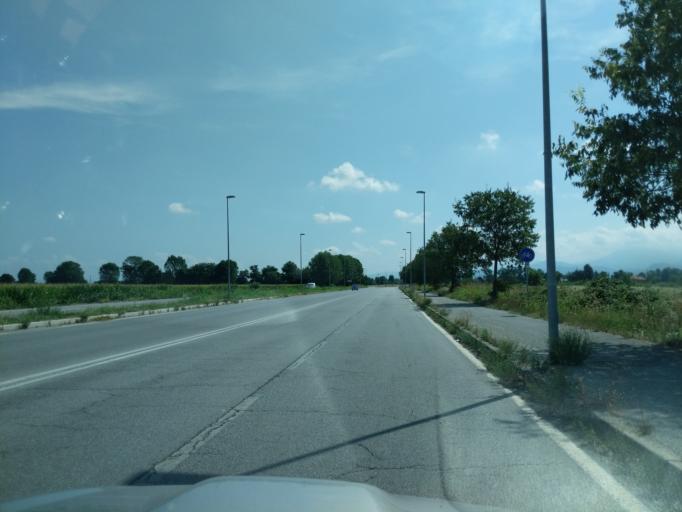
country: IT
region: Piedmont
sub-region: Provincia di Cuneo
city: Cuneo
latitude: 44.3968
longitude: 7.5840
